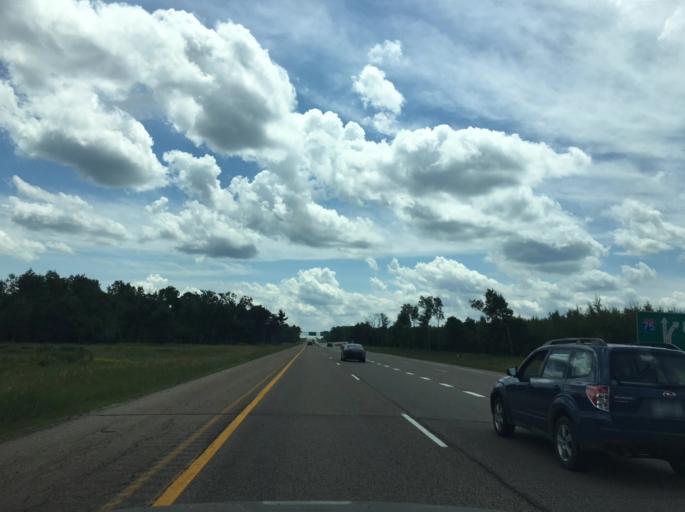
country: US
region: Michigan
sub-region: Crawford County
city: Grayling
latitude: 44.5884
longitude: -84.7097
